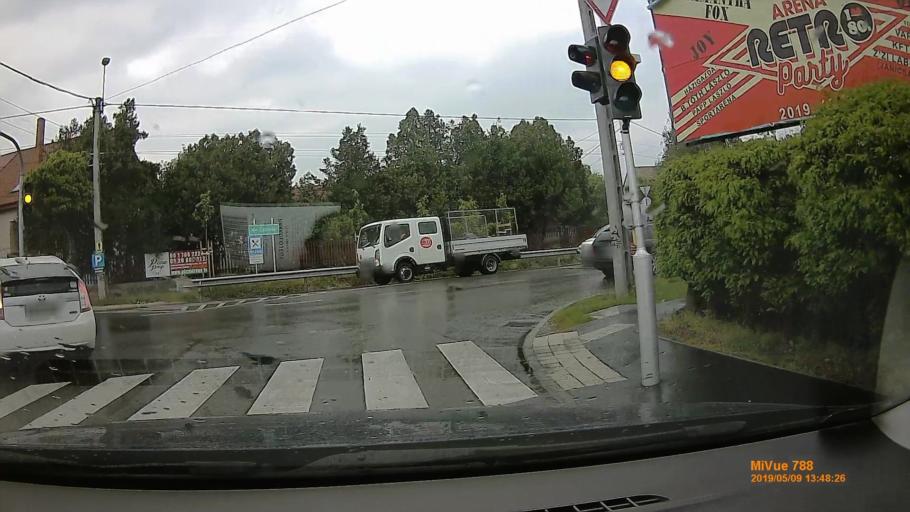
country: HU
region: Budapest
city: Budapest XVI. keruelet
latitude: 47.5312
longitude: 19.1896
